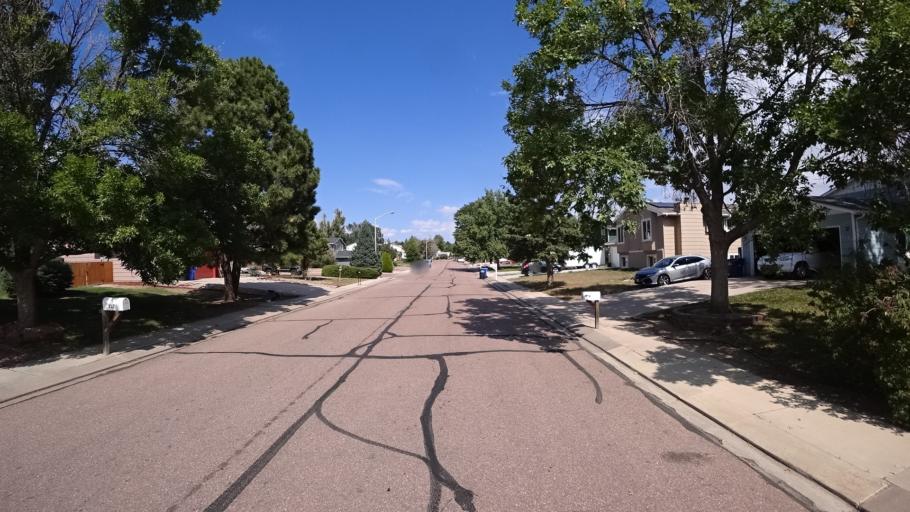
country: US
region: Colorado
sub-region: El Paso County
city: Cimarron Hills
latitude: 38.8636
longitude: -104.7250
